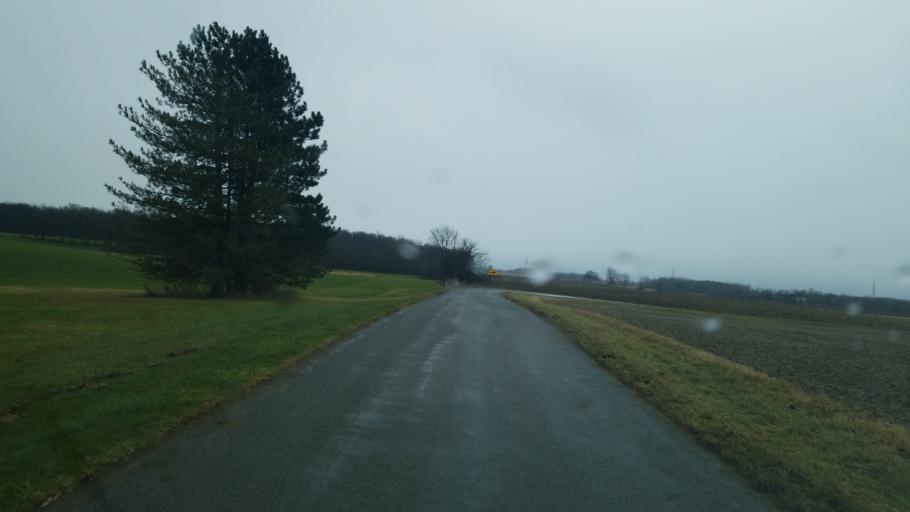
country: US
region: Ohio
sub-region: Hardin County
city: Kenton
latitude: 40.5514
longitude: -83.6538
